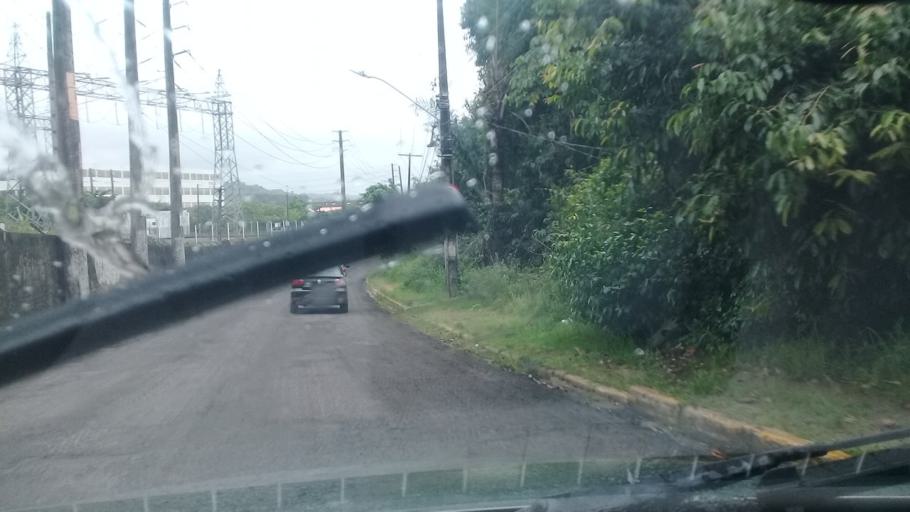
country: BR
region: Pernambuco
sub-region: Jaboatao Dos Guararapes
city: Jaboatao dos Guararapes
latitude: -8.0815
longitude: -34.9799
